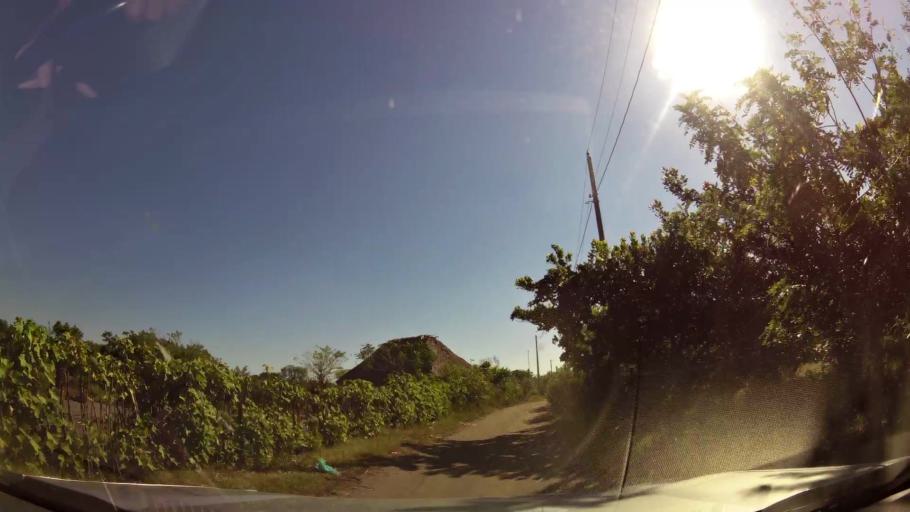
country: GT
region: Jutiapa
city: Pasaco
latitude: 13.8465
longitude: -90.3654
